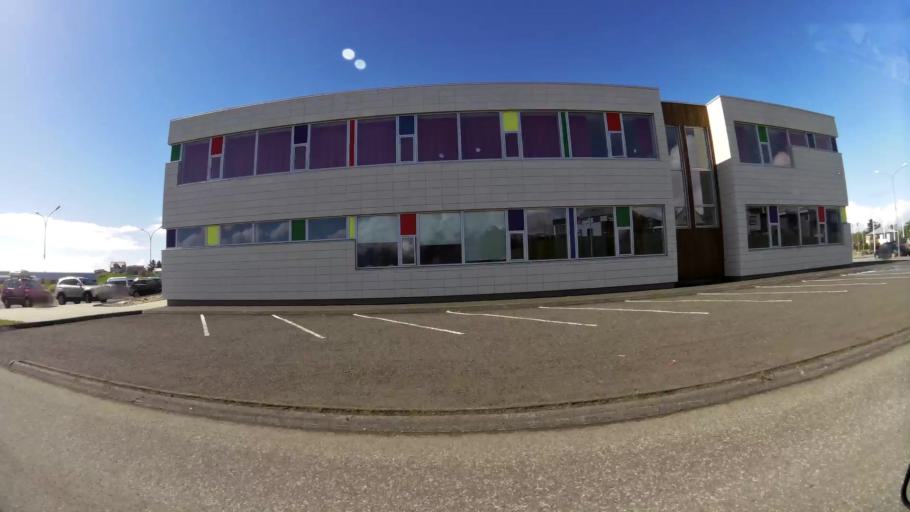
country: IS
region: East
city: Hoefn
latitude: 64.2542
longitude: -15.2068
